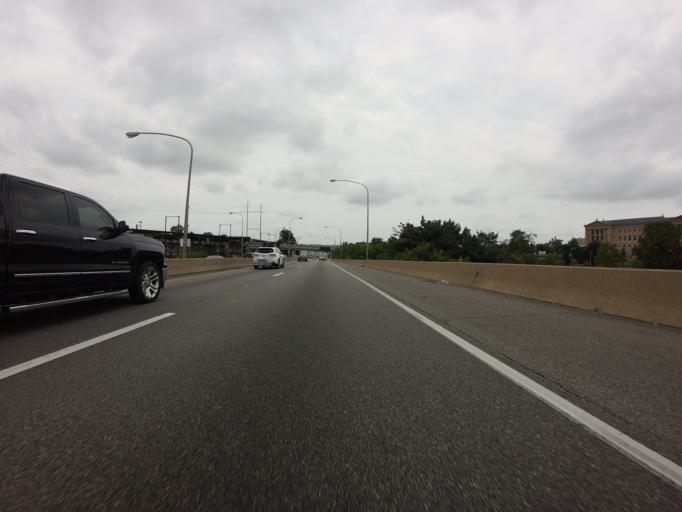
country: US
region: Pennsylvania
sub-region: Philadelphia County
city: Philadelphia
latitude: 39.9625
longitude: -75.1830
